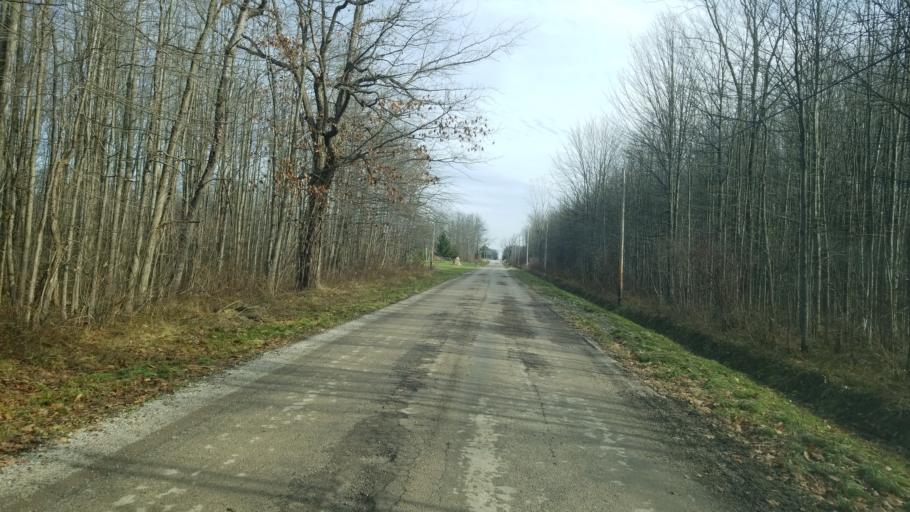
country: US
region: Ohio
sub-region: Ashtabula County
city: Roaming Shores
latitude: 41.6434
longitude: -80.7662
